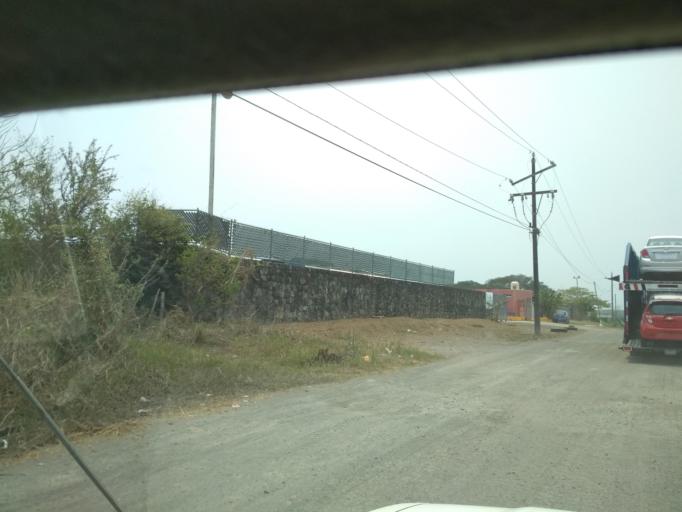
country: MX
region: Veracruz
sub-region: Veracruz
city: Delfino Victoria (Santa Fe)
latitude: 19.2015
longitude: -96.2659
